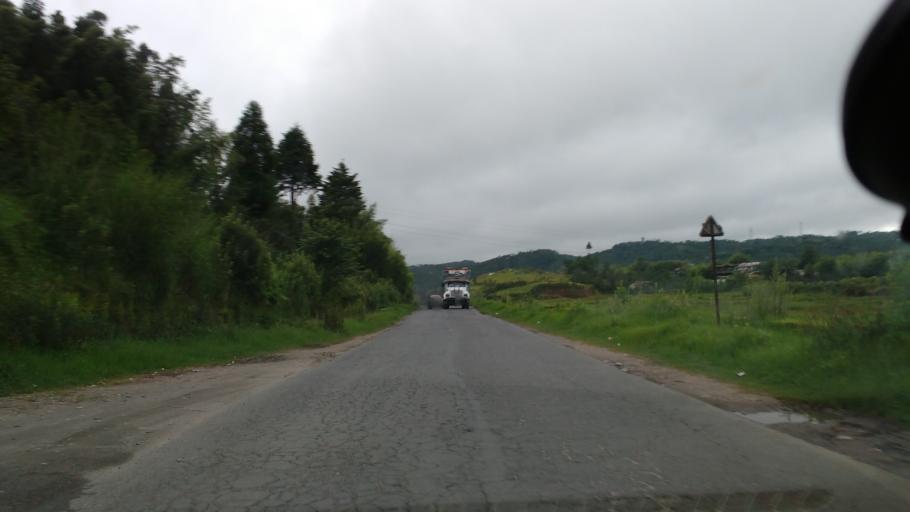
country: IN
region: Meghalaya
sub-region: East Khasi Hills
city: Shillong
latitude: 25.5121
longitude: 91.8120
